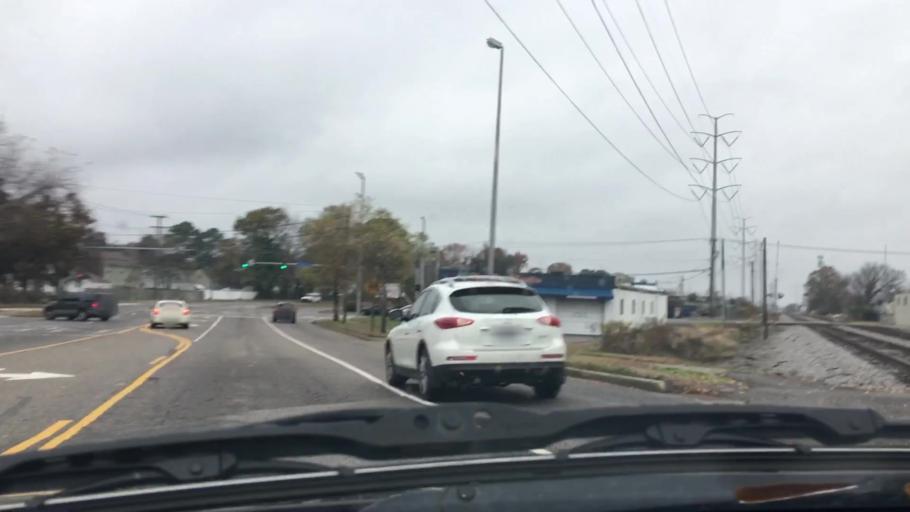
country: US
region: Virginia
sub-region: City of Norfolk
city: Norfolk
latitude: 36.8674
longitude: -76.2491
